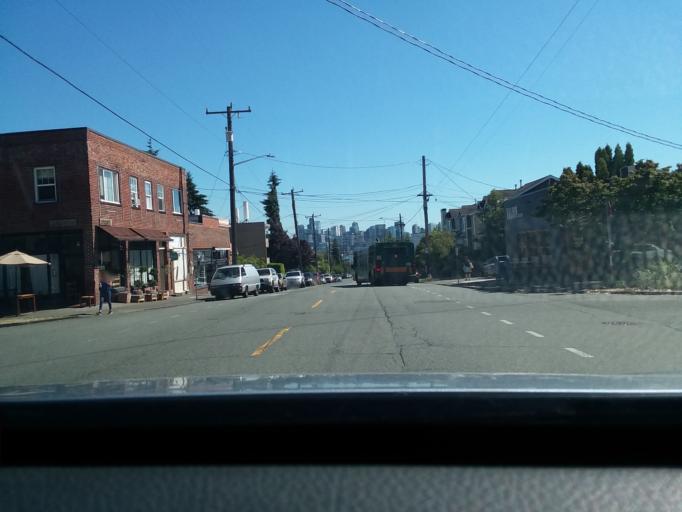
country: US
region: Washington
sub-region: King County
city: Seattle
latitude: 47.6521
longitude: -122.3364
